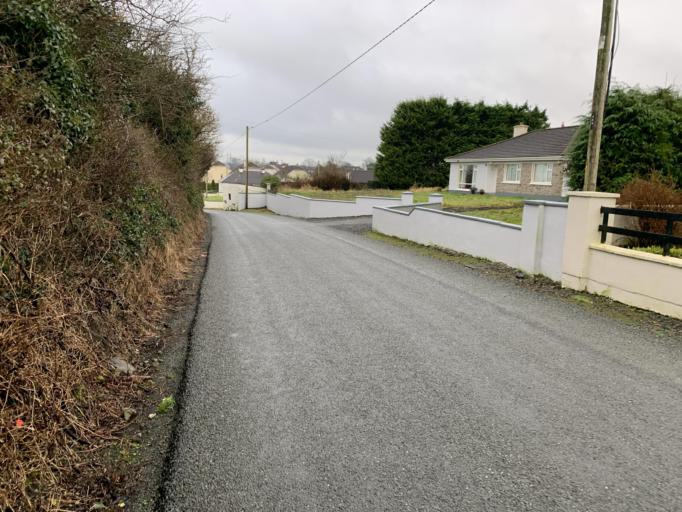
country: IE
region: Connaught
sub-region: County Galway
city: Tuam
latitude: 53.5135
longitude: -8.8714
